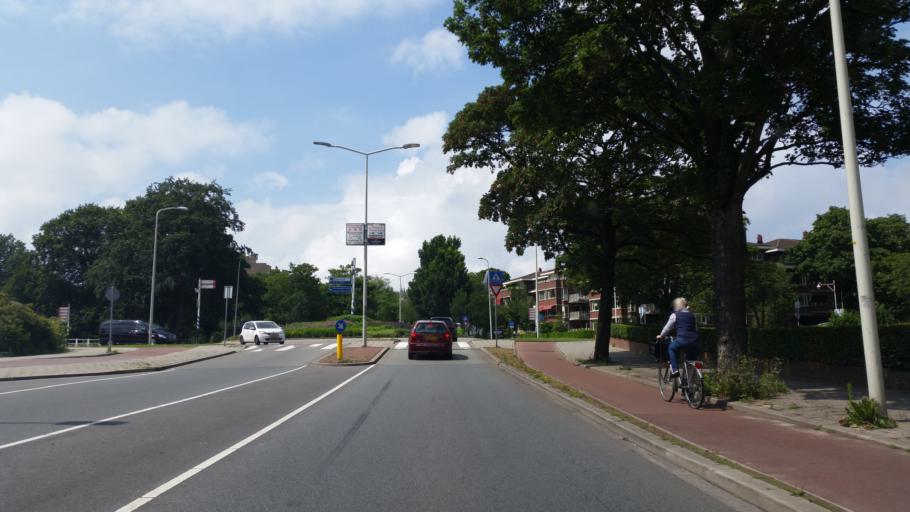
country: NL
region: South Holland
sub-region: Gemeente Den Haag
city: The Hague
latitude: 52.0992
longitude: 4.3016
